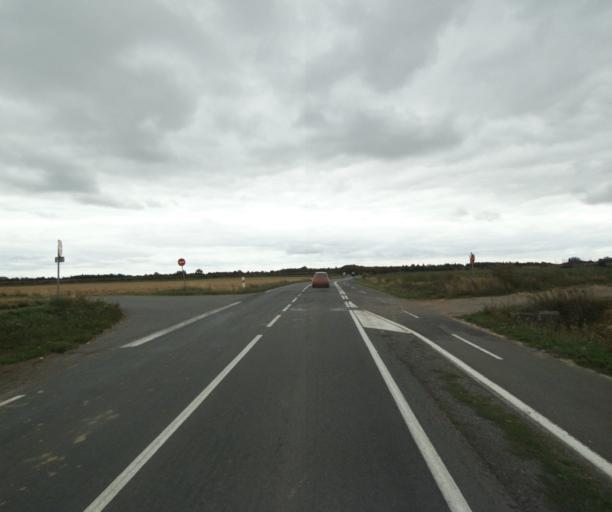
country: FR
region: Nord-Pas-de-Calais
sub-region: Departement du Nord
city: Lesquin
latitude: 50.5678
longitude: 3.1244
